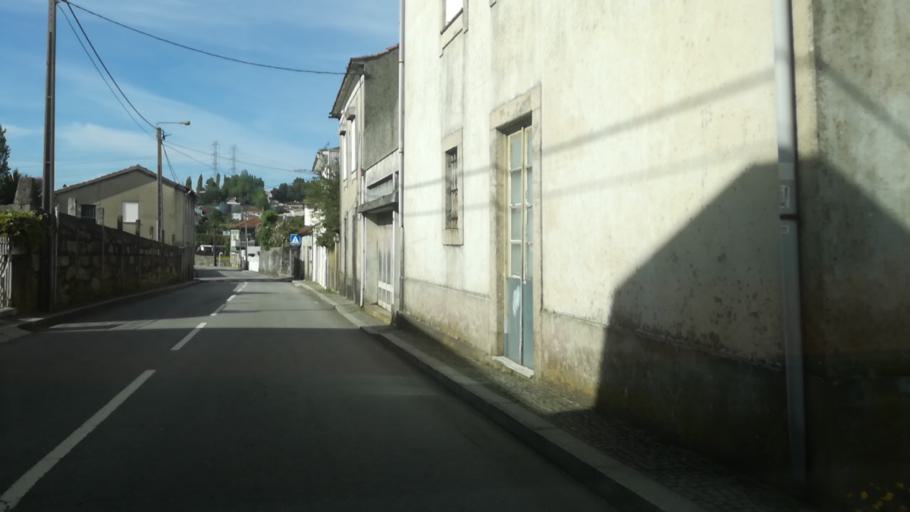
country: PT
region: Porto
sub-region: Maia
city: Nogueira
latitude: 41.2307
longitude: -8.5873
